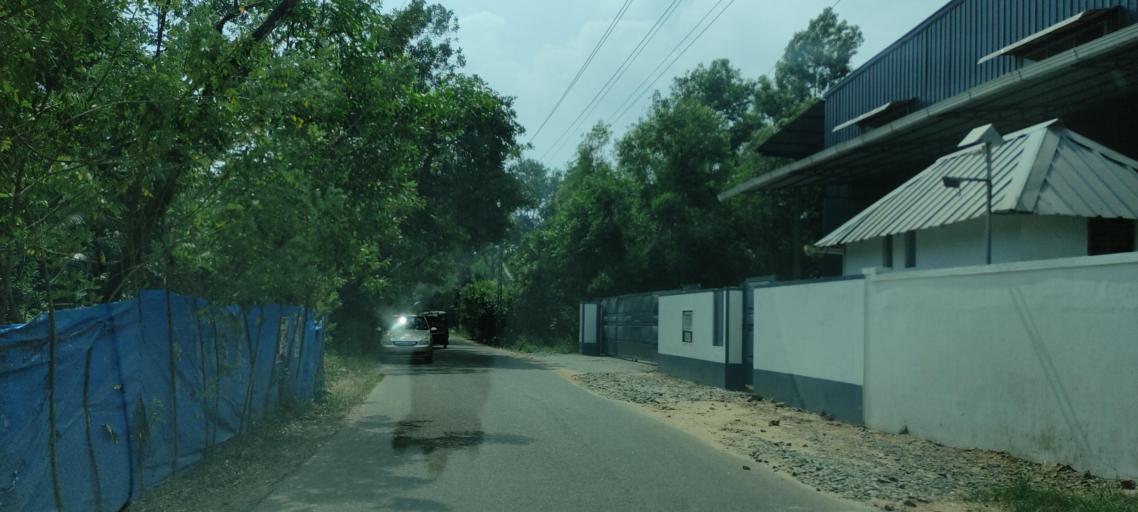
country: IN
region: Kerala
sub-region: Alappuzha
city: Shertallai
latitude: 9.6289
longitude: 76.3512
